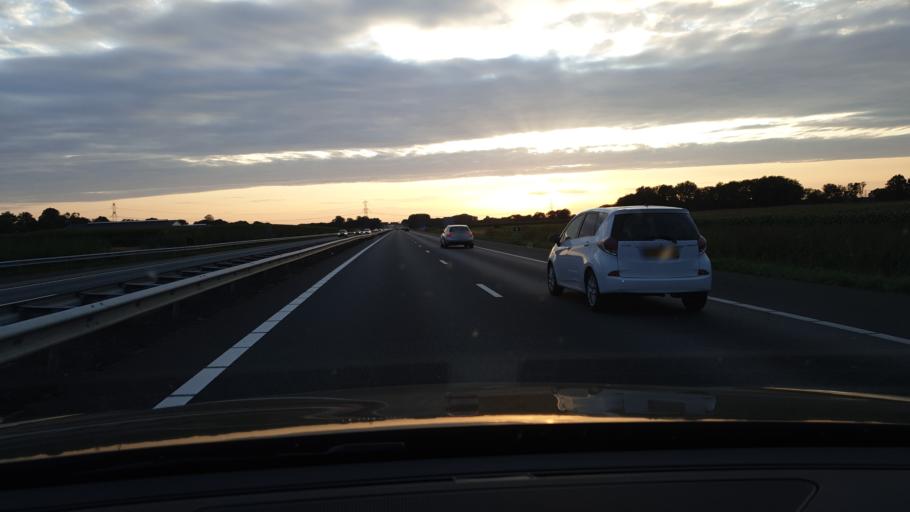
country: NL
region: North Brabant
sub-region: Gemeente Asten
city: Asten
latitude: 51.4206
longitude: 5.7204
